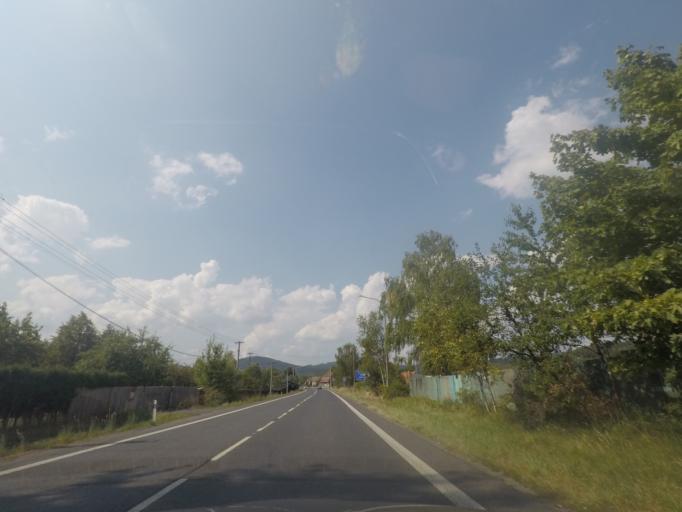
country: CZ
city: Cvikov
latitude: 50.7797
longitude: 14.6223
